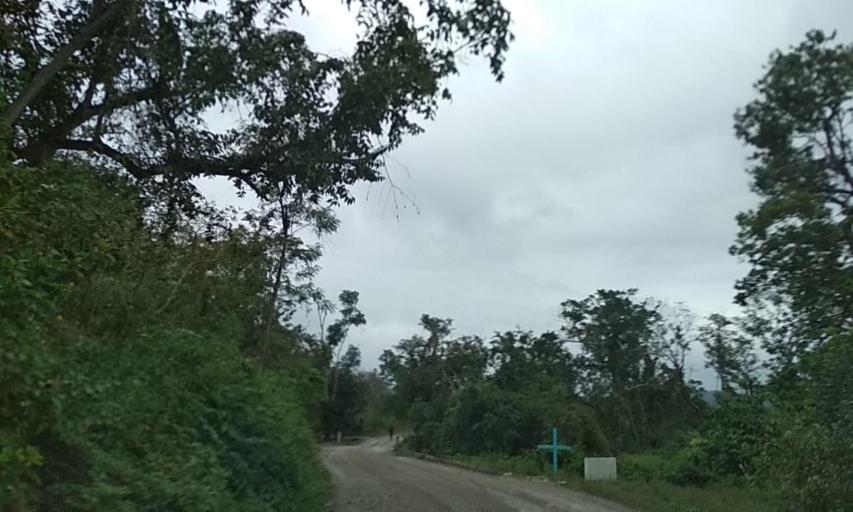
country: MX
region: Veracruz
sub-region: Papantla
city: El Chote
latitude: 20.3857
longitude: -97.3524
